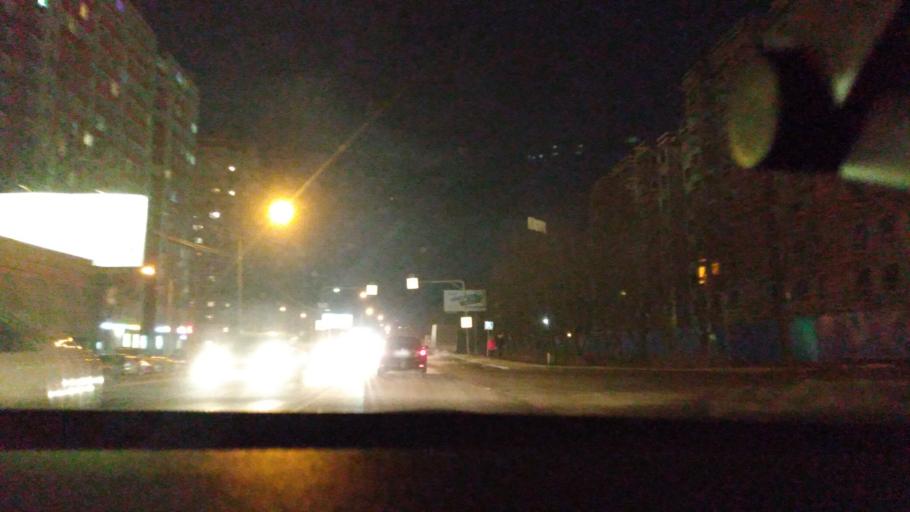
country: RU
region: Moskovskaya
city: Shchelkovo
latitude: 55.9377
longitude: 37.9741
